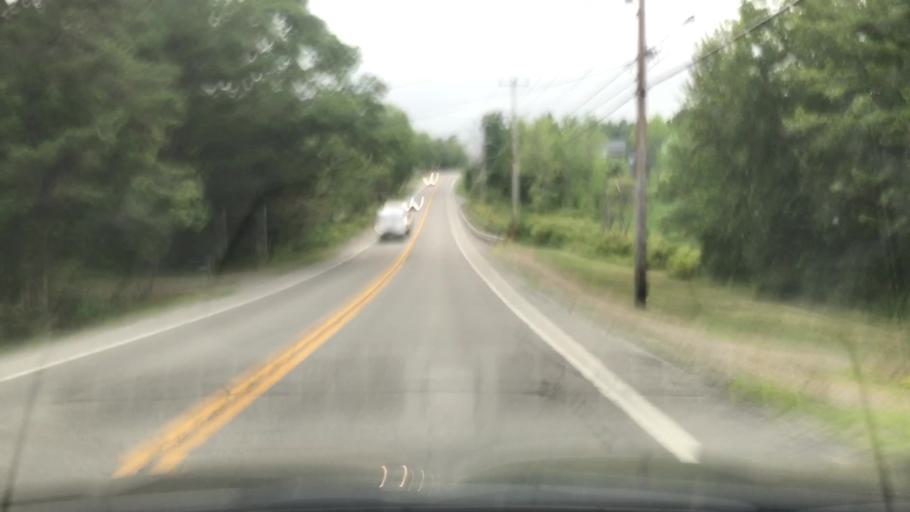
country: US
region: Maine
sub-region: Hancock County
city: Trenton
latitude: 44.4046
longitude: -68.3432
